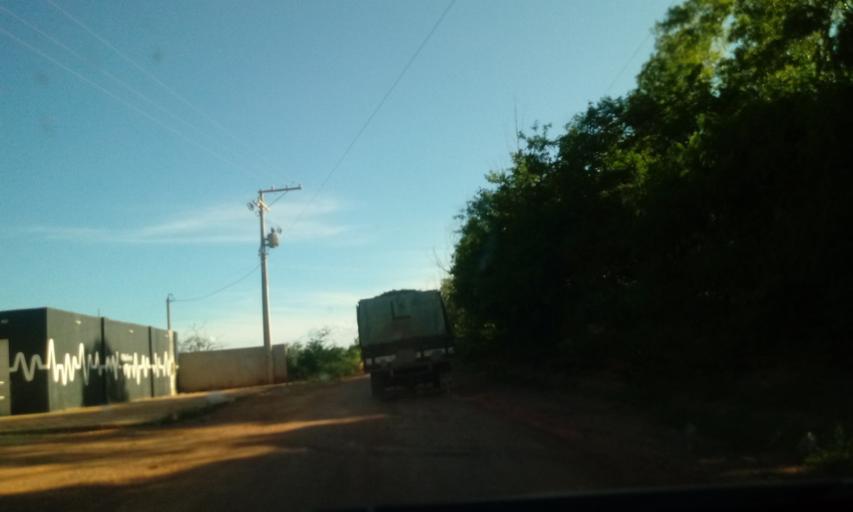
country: BR
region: Bahia
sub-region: Riacho De Santana
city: Riacho de Santana
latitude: -13.7809
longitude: -42.7232
